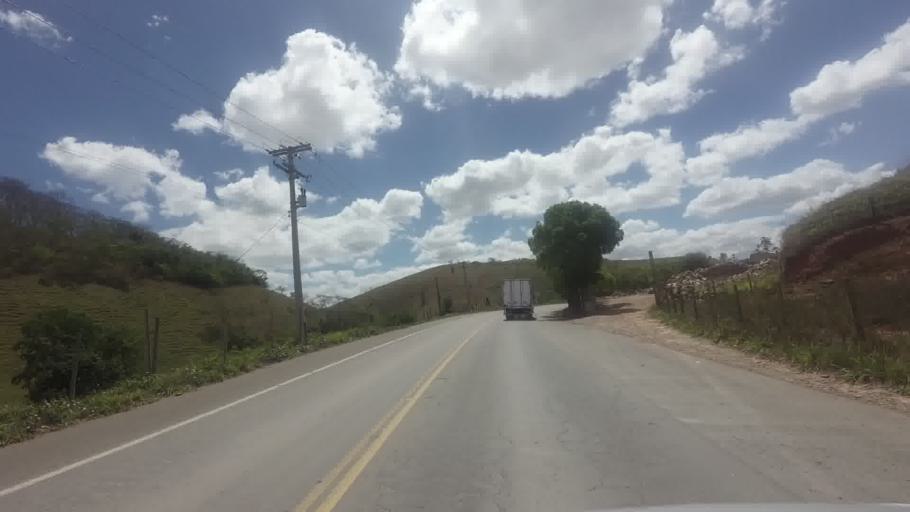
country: BR
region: Rio de Janeiro
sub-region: Santo Antonio De Padua
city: Santo Antonio de Padua
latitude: -21.6333
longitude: -42.2696
